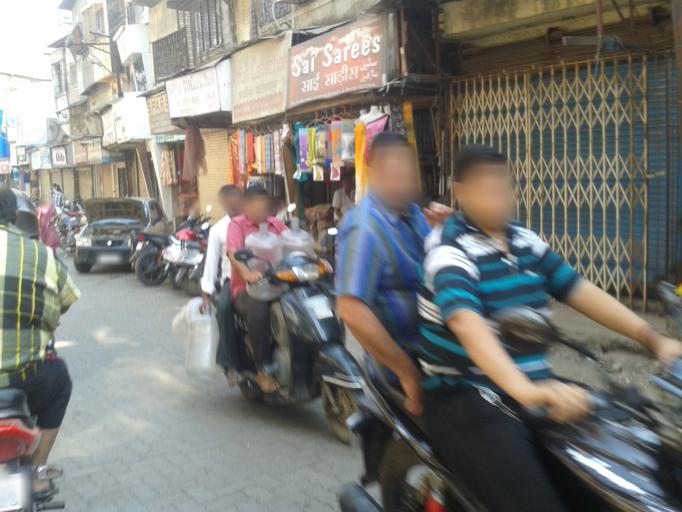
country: IN
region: Maharashtra
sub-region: Thane
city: Ulhasnagar
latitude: 19.2365
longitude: 73.1646
